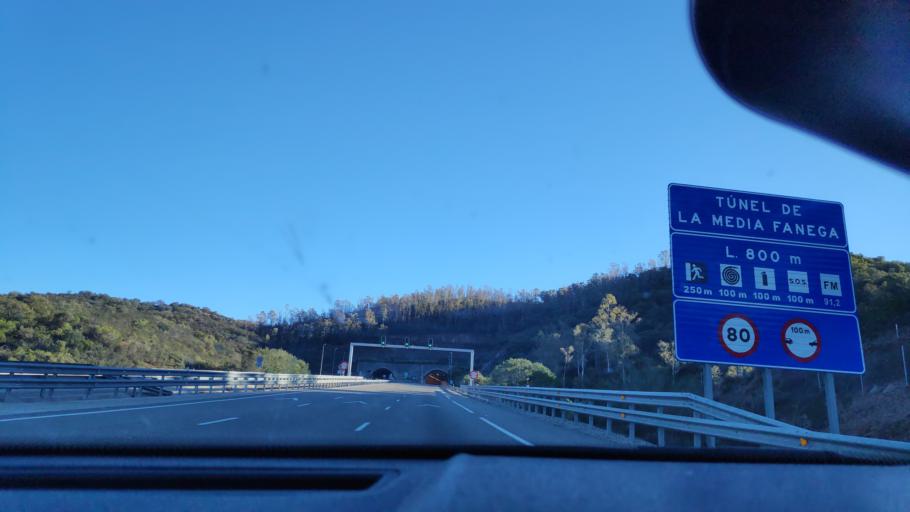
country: ES
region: Andalusia
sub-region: Provincia de Sevilla
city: El Ronquillo
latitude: 37.6532
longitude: -6.1623
